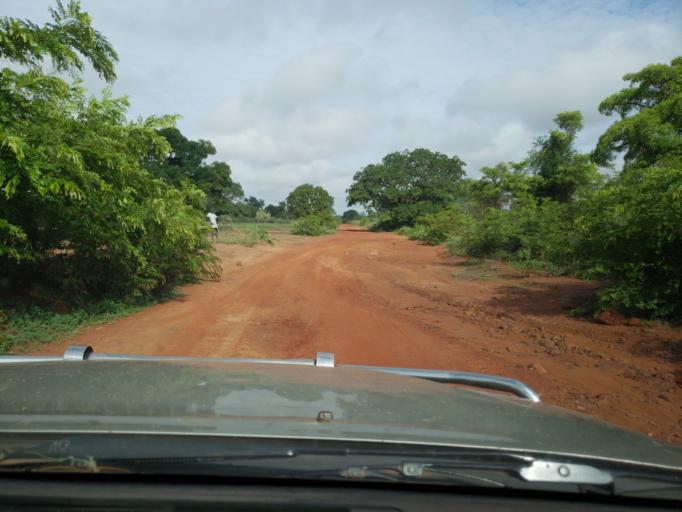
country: ML
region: Sikasso
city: Koutiala
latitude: 12.3924
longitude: -6.0005
